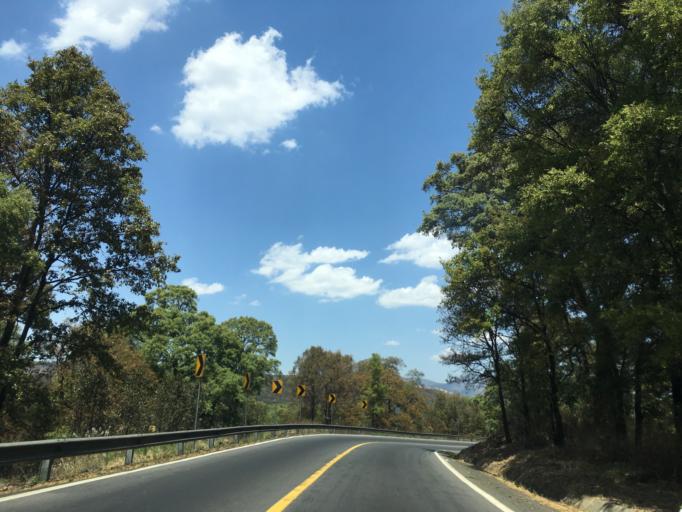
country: MX
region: Mexico
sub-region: Chalco
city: Zopoco
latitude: 19.7961
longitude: -102.0266
